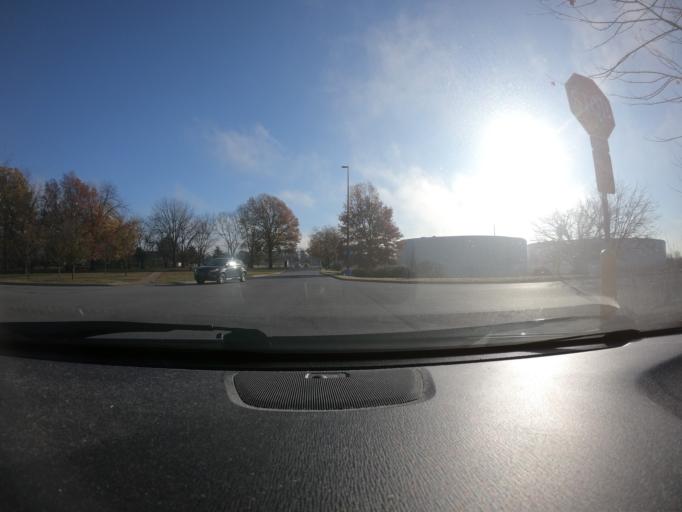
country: US
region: Arkansas
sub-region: Benton County
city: Bentonville
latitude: 36.3681
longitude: -94.2234
